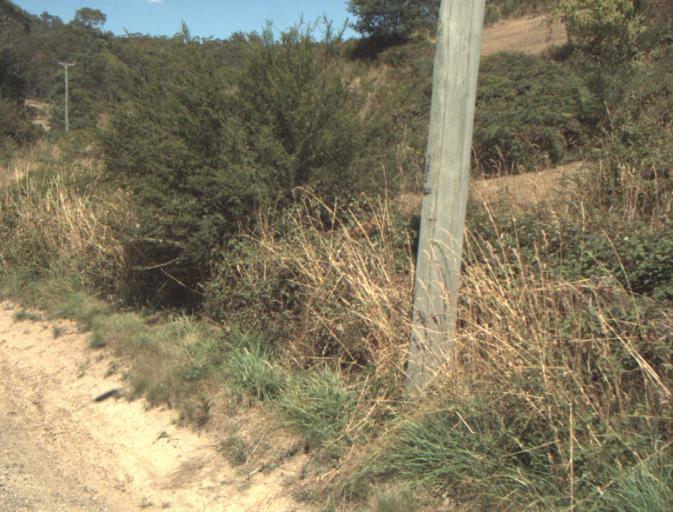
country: AU
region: Tasmania
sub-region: Launceston
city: Mayfield
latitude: -41.2683
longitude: 147.1329
